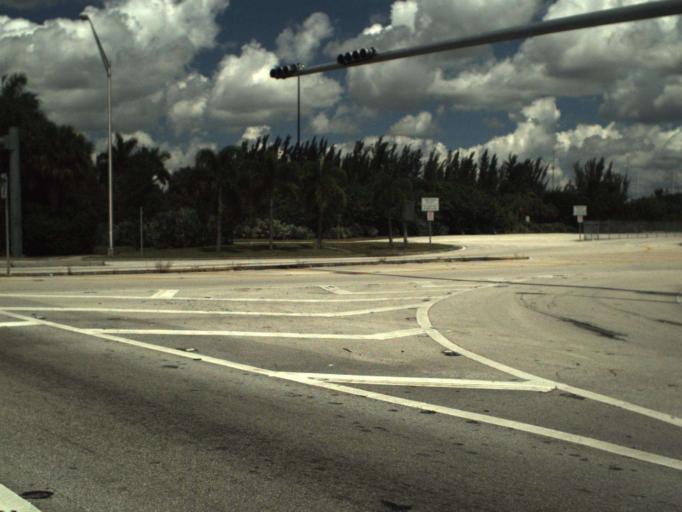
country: US
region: Florida
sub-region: Miami-Dade County
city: Golden Glades
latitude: 25.9215
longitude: -80.2129
